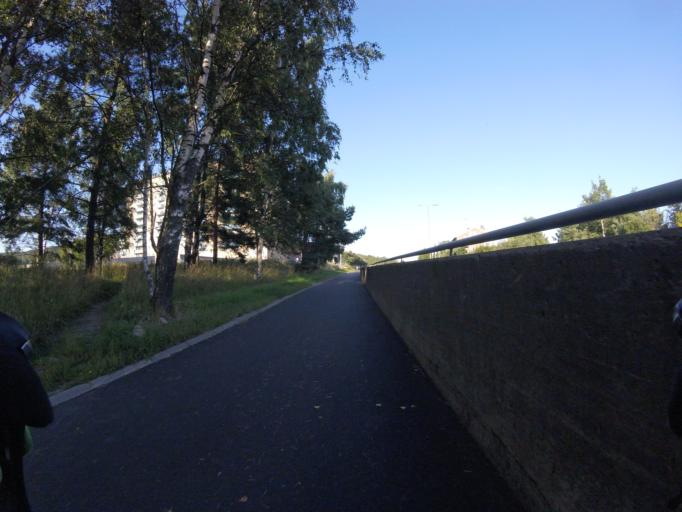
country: NO
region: Akershus
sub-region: Lorenskog
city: Kjenn
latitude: 59.9595
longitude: 10.8794
